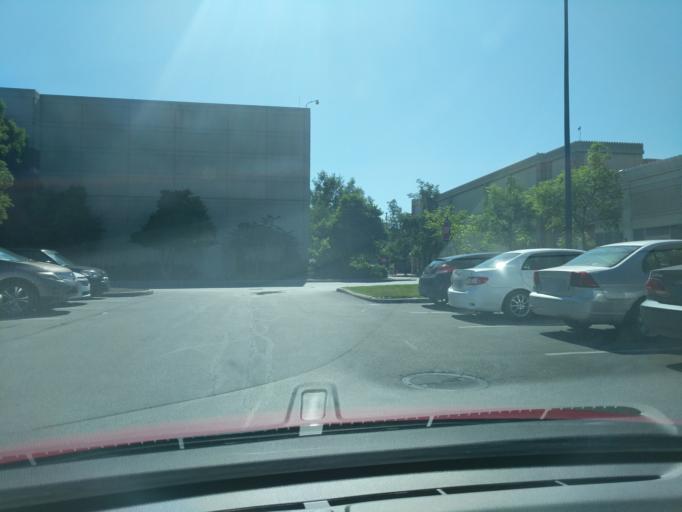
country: US
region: Ohio
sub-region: Franklin County
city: Huber Ridge
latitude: 40.0546
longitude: -82.9162
